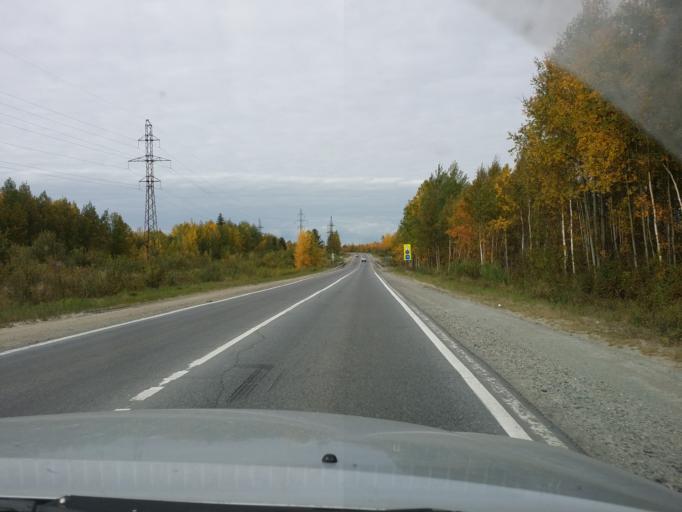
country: RU
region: Khanty-Mansiyskiy Avtonomnyy Okrug
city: Megion
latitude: 61.1066
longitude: 75.9169
